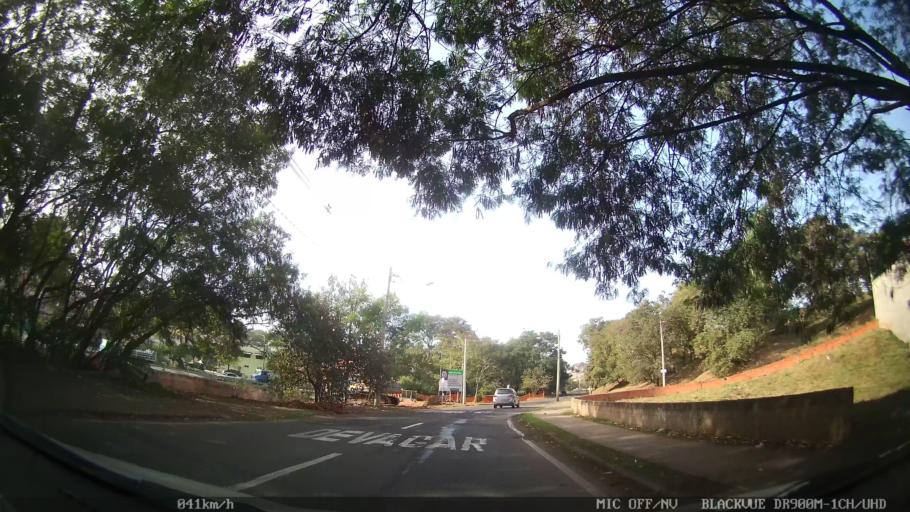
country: BR
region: Sao Paulo
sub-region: Piracicaba
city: Piracicaba
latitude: -22.7352
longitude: -47.6692
